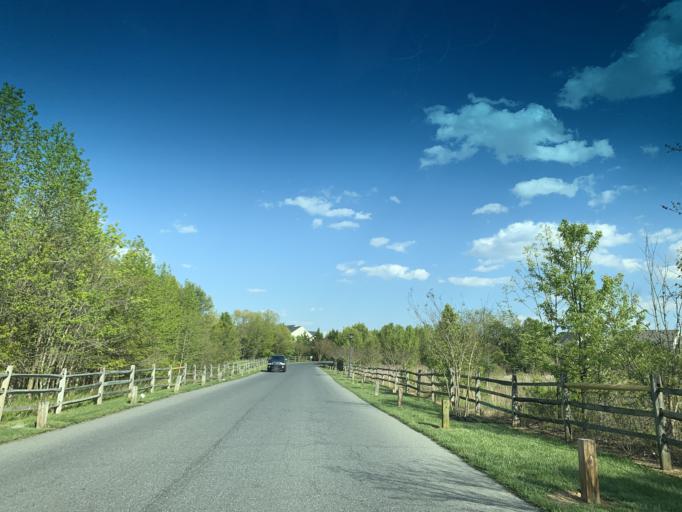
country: US
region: Maryland
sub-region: Baltimore County
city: White Marsh
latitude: 39.4076
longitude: -76.4343
